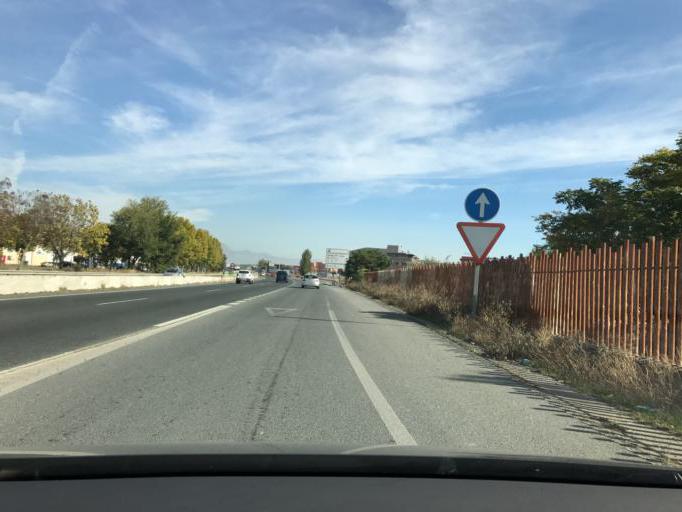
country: ES
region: Andalusia
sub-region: Provincia de Granada
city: Chauchina
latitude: 37.1900
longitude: -3.7328
